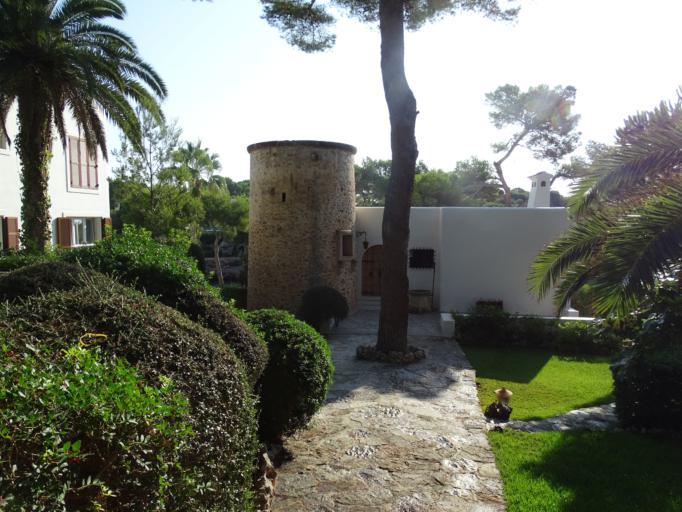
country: ES
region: Balearic Islands
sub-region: Illes Balears
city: Santanyi
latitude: 39.3701
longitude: 3.2294
